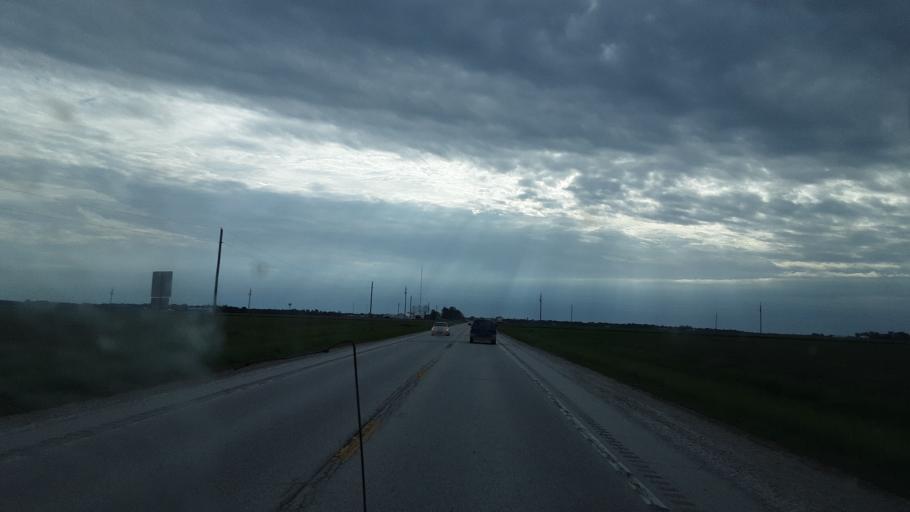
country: US
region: Illinois
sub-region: Hancock County
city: Carthage
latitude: 40.4052
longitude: -91.1825
